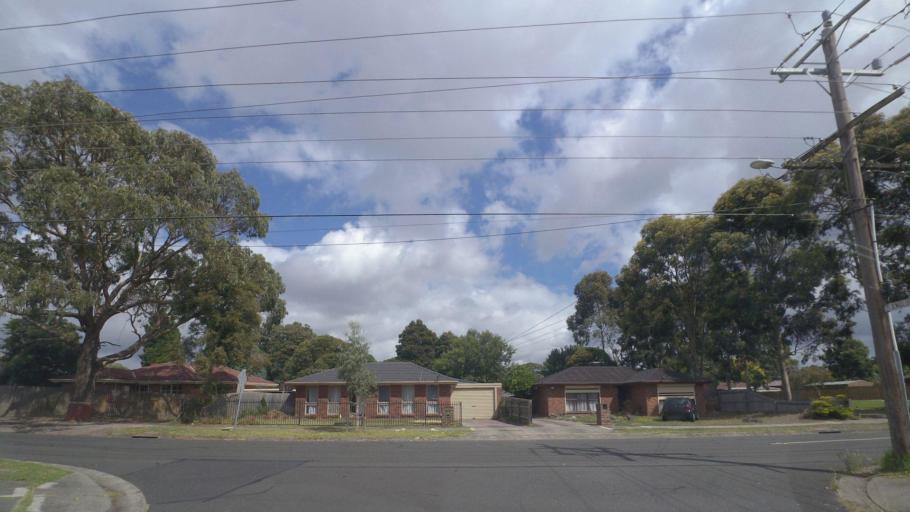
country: AU
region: Victoria
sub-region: Knox
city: Scoresby
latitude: -37.8954
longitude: 145.2290
